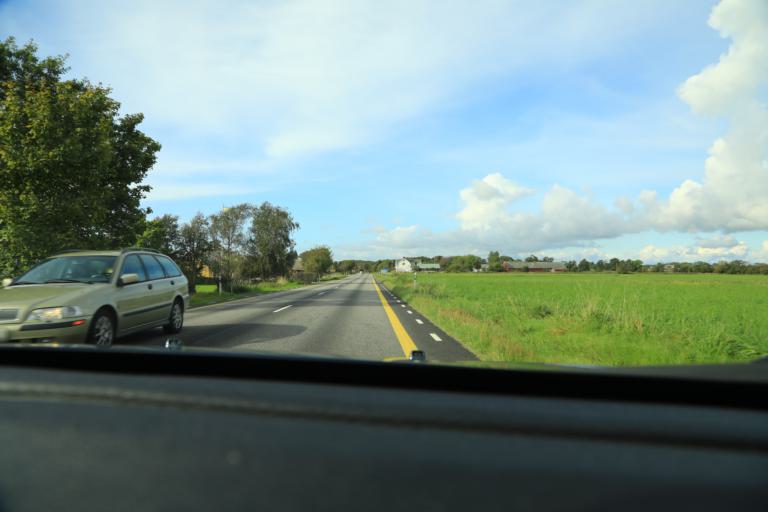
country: SE
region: Halland
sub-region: Varbergs Kommun
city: Traslovslage
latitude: 57.0337
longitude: 12.3286
